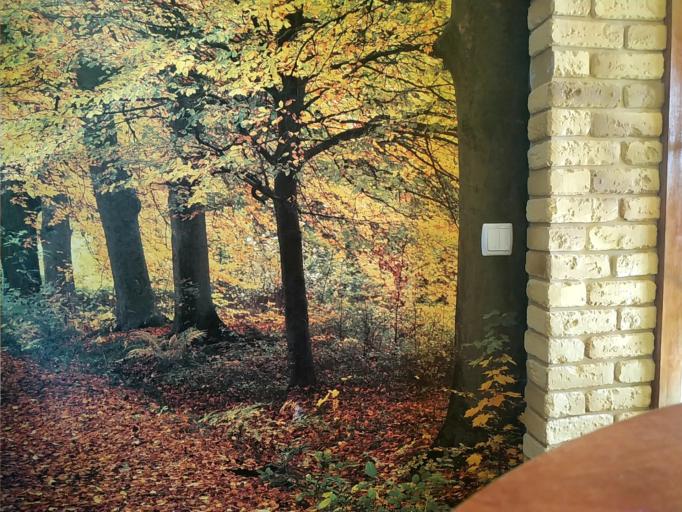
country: RU
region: Jaroslavl
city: Kukoboy
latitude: 58.8452
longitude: 39.7426
